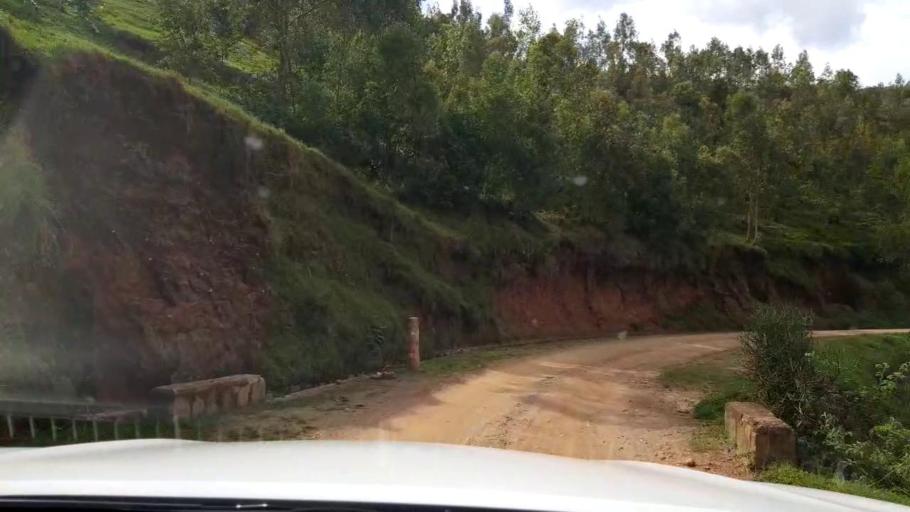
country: RW
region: Southern Province
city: Gitarama
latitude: -1.9954
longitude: 29.7083
